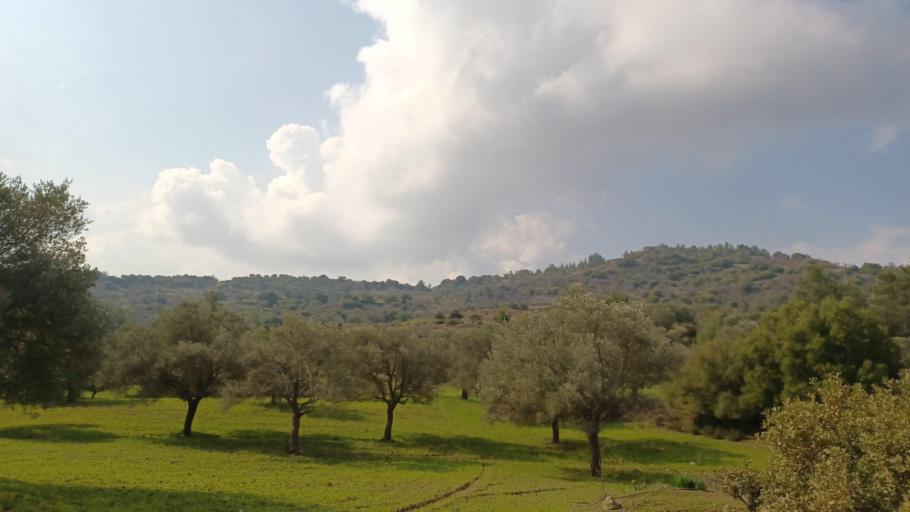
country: CY
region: Pafos
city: Polis
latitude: 34.9964
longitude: 32.5333
